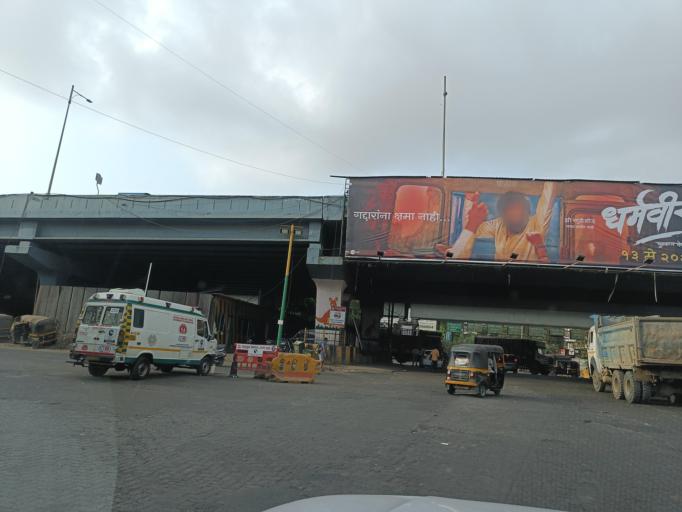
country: IN
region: Maharashtra
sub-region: Thane
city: Thane
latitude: 19.2123
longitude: 72.9774
